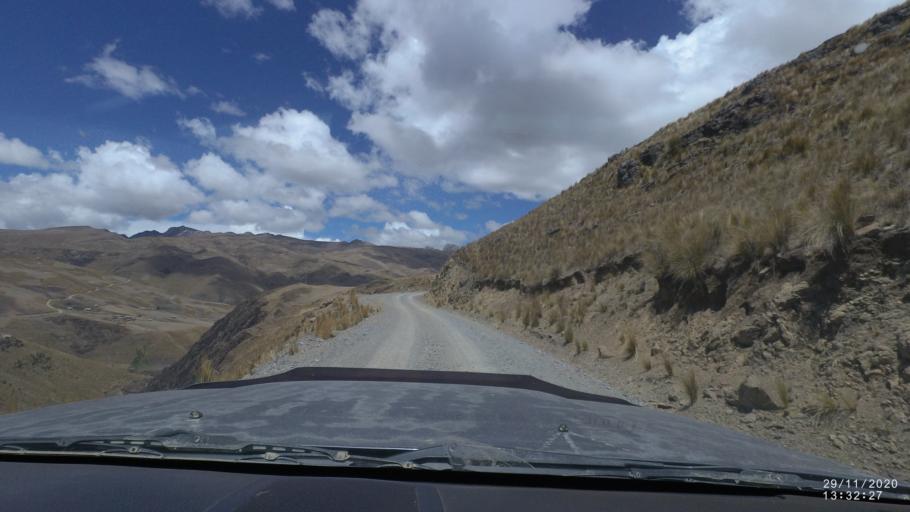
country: BO
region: Cochabamba
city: Cochabamba
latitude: -17.1066
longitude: -66.3419
